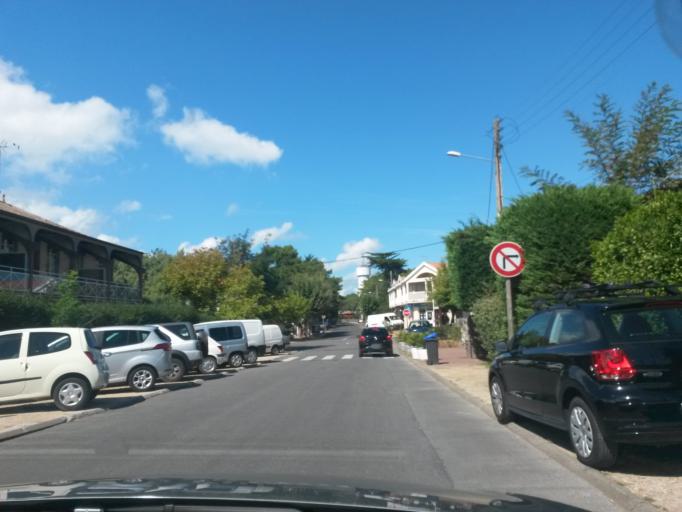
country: FR
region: Aquitaine
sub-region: Departement de la Gironde
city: Arcachon
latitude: 44.6477
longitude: -1.2488
